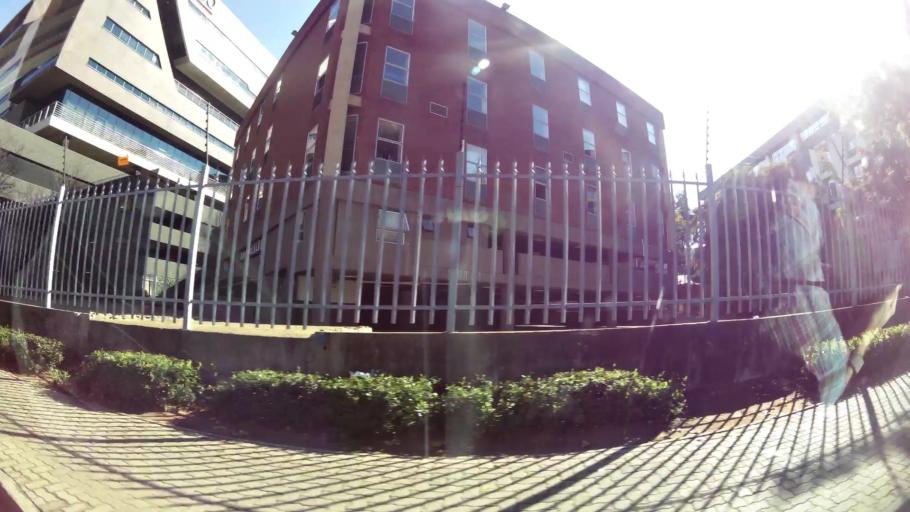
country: ZA
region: Gauteng
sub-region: City of Johannesburg Metropolitan Municipality
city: Johannesburg
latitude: -26.1854
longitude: 28.0375
